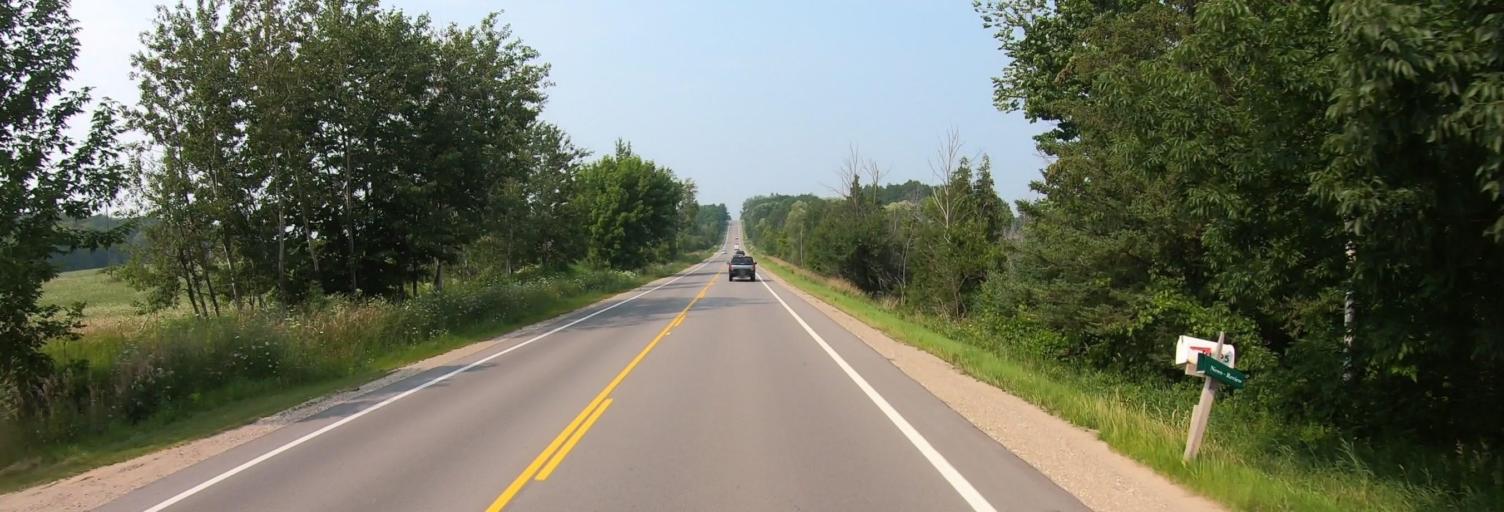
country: US
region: Michigan
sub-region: Charlevoix County
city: Charlevoix
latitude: 45.2357
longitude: -85.2612
